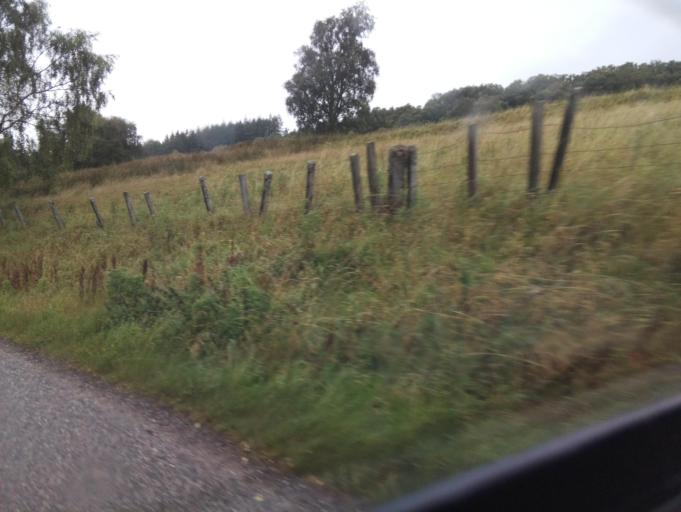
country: GB
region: Scotland
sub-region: Highland
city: Grantown on Spey
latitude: 57.2668
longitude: -3.4134
